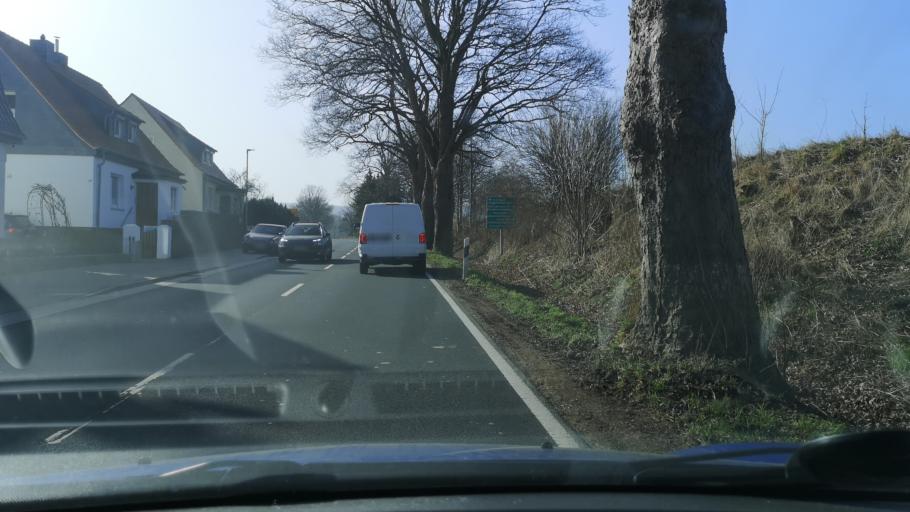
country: DE
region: Lower Saxony
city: Salzhemmendorf
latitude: 52.0829
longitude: 9.5986
